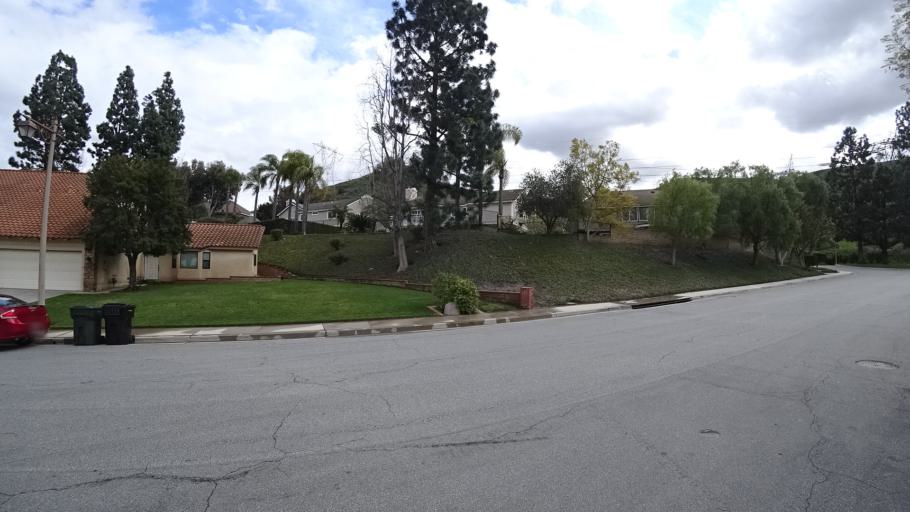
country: US
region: California
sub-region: Orange County
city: Villa Park
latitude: 33.8389
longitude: -117.7865
